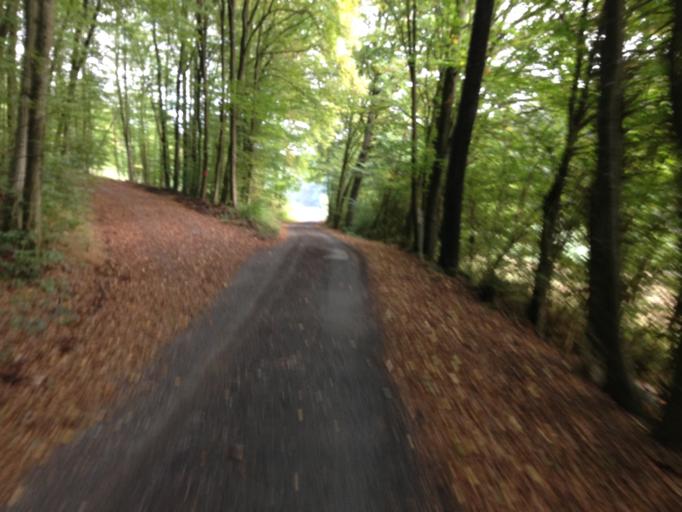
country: DE
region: Hesse
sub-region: Regierungsbezirk Giessen
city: Heuchelheim
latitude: 50.6457
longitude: 8.5621
